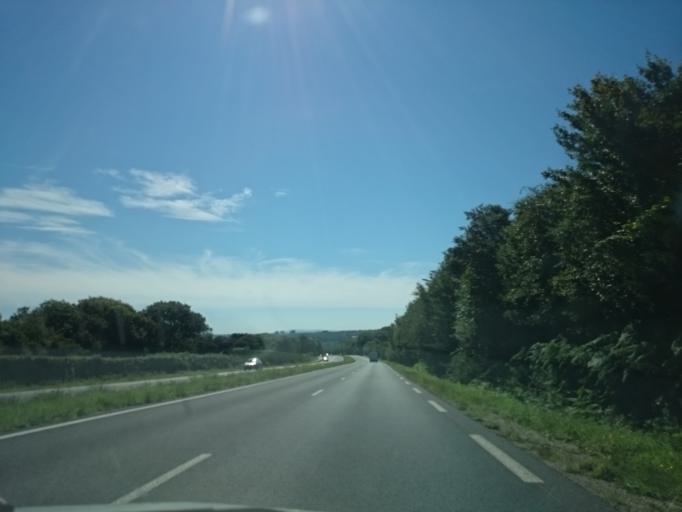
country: FR
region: Brittany
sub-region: Departement du Finistere
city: Guilers
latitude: 48.4153
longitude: -4.5443
